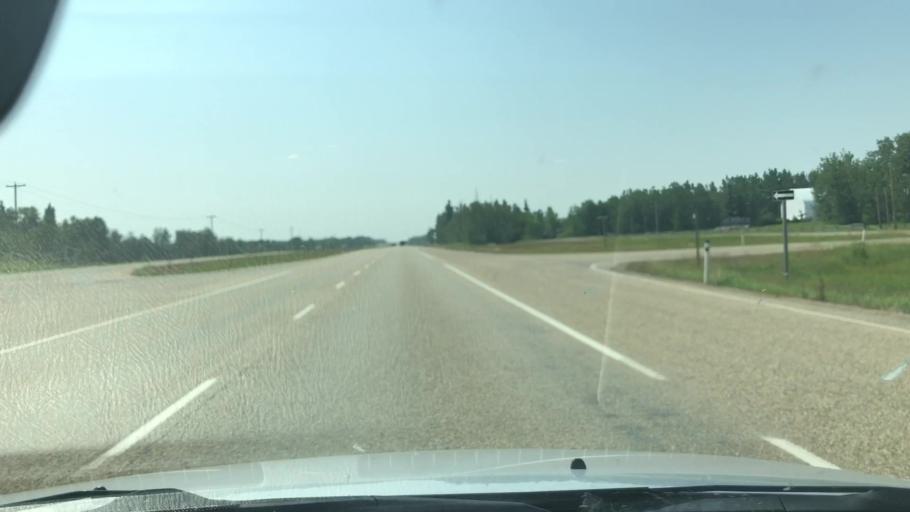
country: CA
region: Alberta
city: Devon
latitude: 53.4363
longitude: -113.7635
